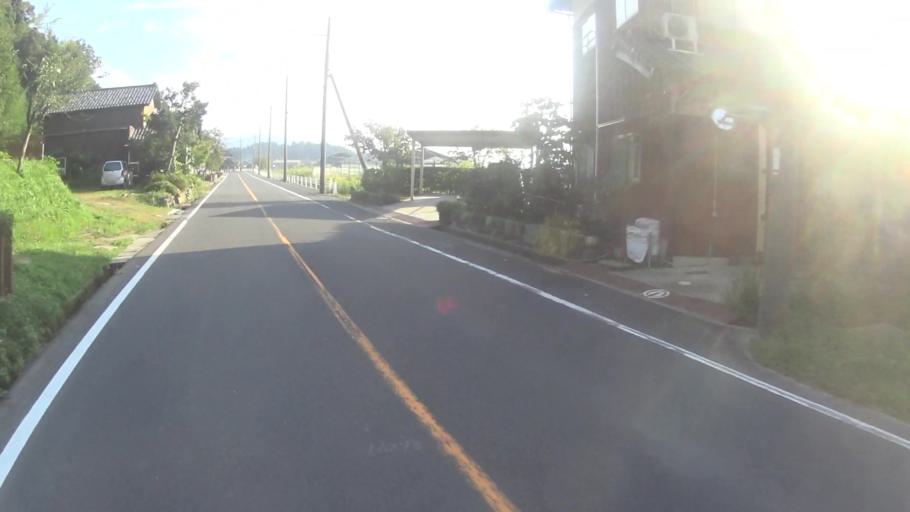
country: JP
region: Kyoto
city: Miyazu
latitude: 35.6868
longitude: 135.0981
